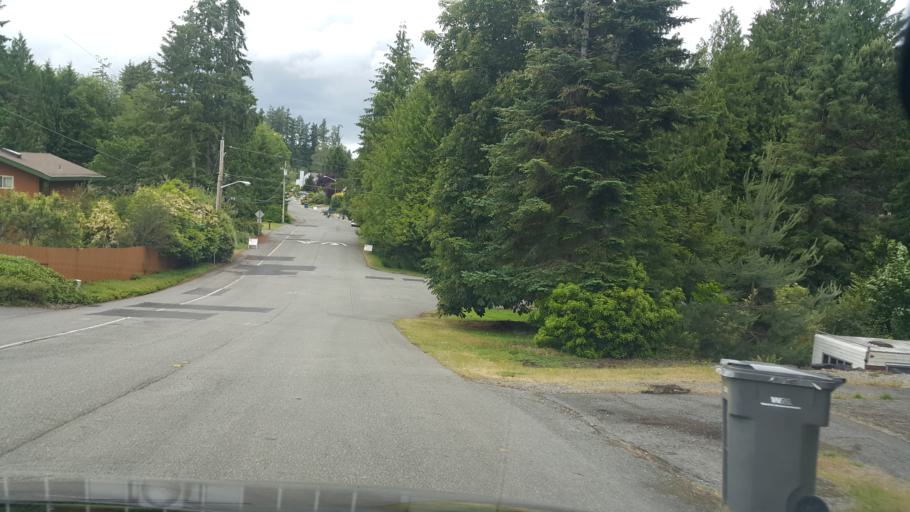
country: US
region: Washington
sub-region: King County
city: Fairwood
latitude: 47.4383
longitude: -122.1475
